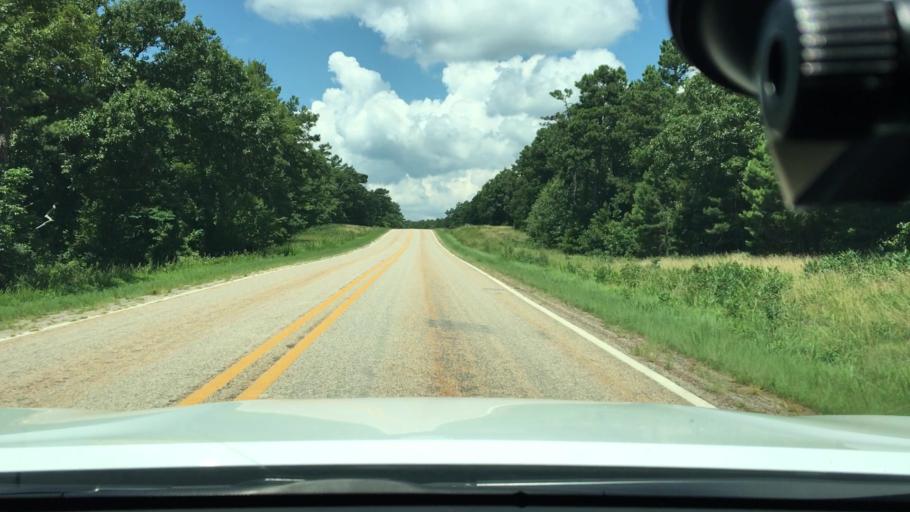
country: US
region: Arkansas
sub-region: Logan County
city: Paris
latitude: 35.1762
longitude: -93.5975
